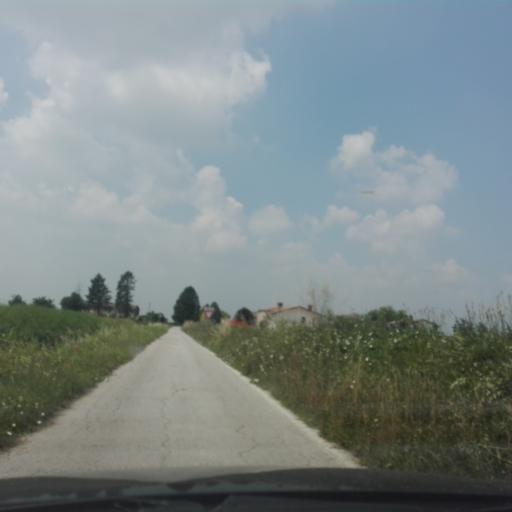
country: IT
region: Veneto
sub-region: Provincia di Rovigo
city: Villanova Marchesana
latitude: 44.9910
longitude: 11.9490
